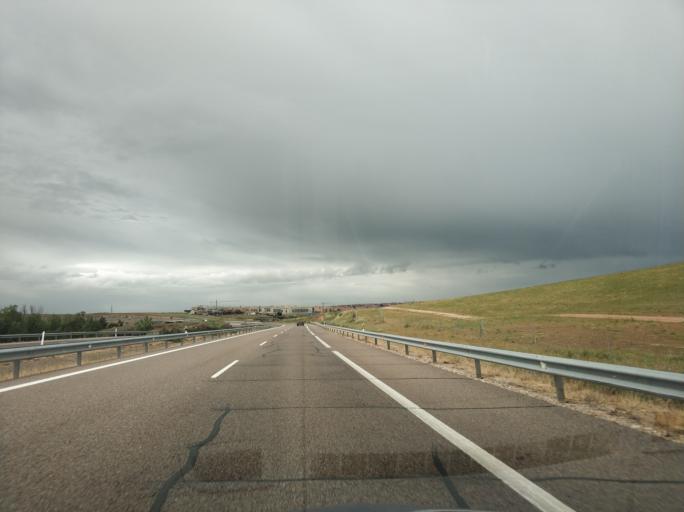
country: ES
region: Castille and Leon
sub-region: Provincia de Salamanca
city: Aldeatejada
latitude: 40.9339
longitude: -5.6798
